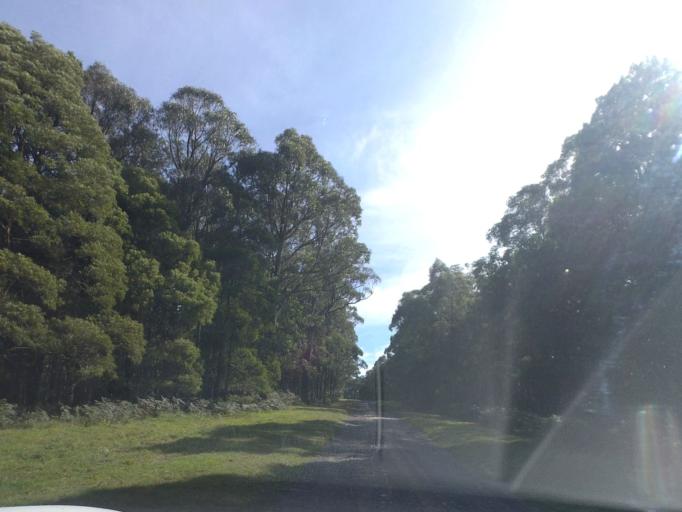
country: AU
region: Victoria
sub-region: Moorabool
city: Bacchus Marsh
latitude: -37.4616
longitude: 144.2154
